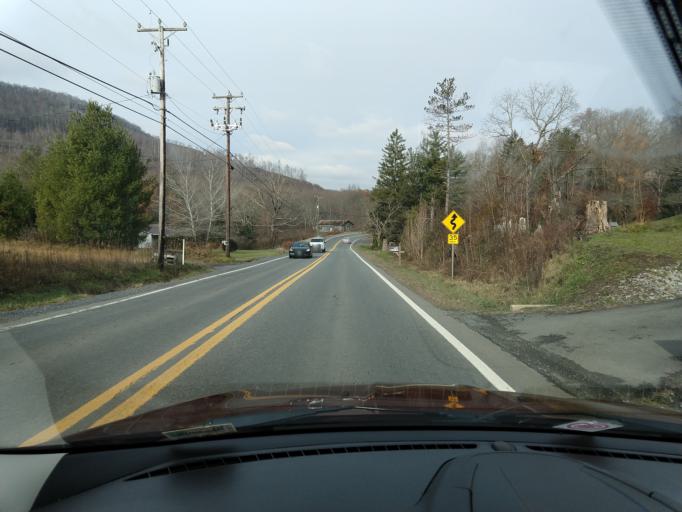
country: US
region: West Virginia
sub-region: Greenbrier County
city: Rainelle
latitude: 37.9711
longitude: -80.7064
